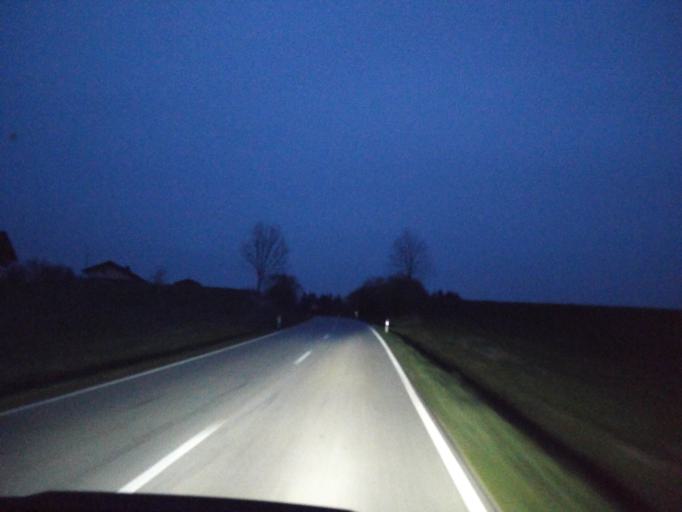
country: DE
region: Bavaria
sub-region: Upper Bavaria
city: Schonstett
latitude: 47.9795
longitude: 12.2130
